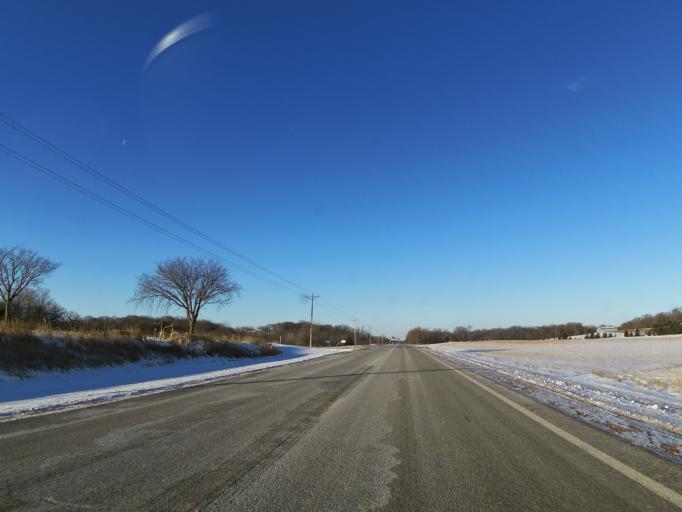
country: US
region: Minnesota
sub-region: Le Sueur County
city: New Prague
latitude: 44.6306
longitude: -93.5237
